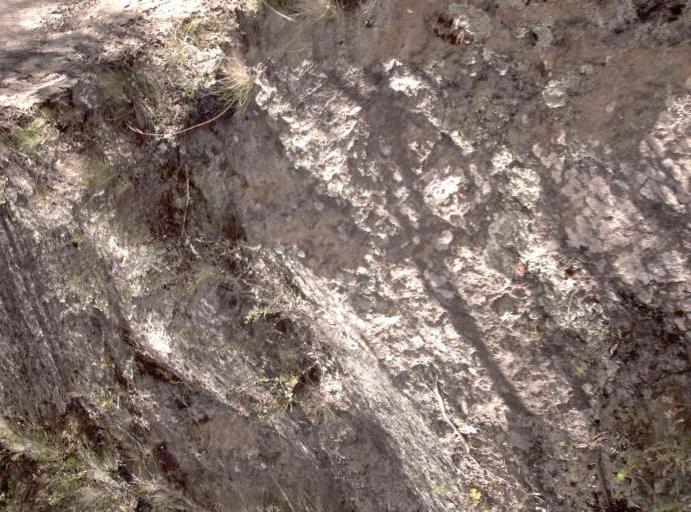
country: AU
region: New South Wales
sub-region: Snowy River
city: Jindabyne
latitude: -37.0873
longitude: 148.3306
